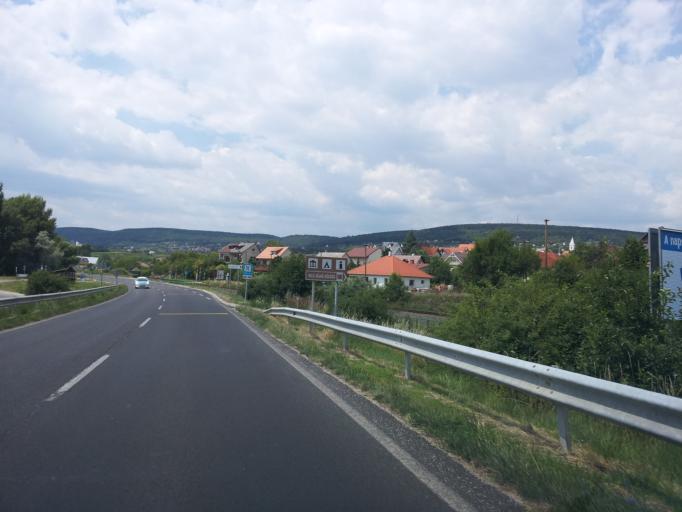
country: HU
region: Veszprem
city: Csopak
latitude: 46.9794
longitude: 17.9461
